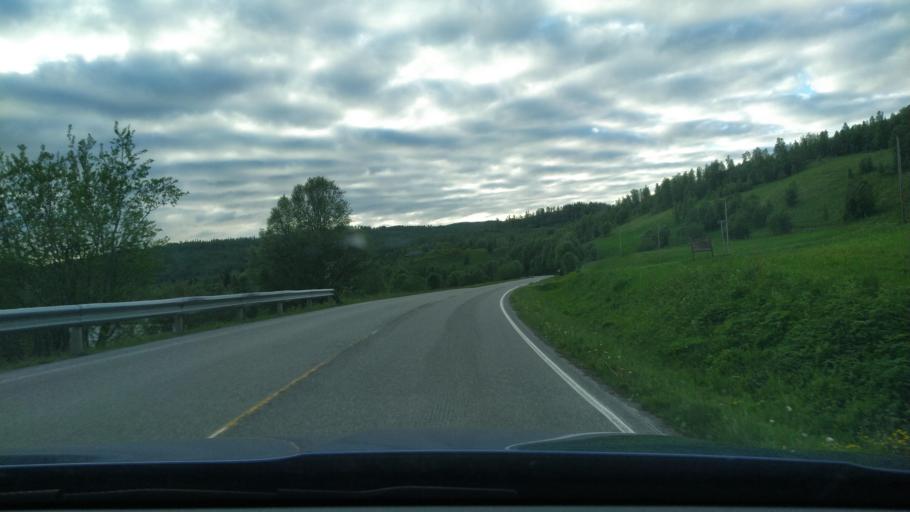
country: NO
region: Troms
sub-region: Sorreisa
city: Sorreisa
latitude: 69.0923
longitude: 18.3411
